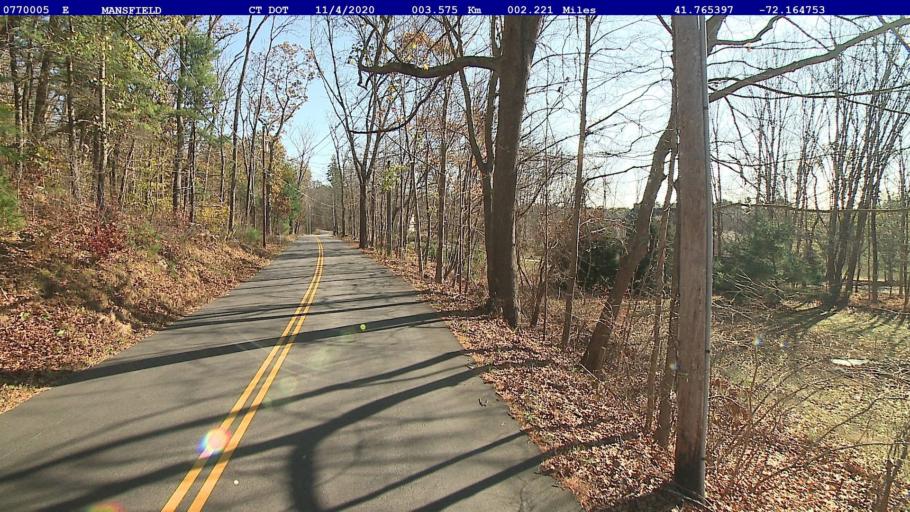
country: US
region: Connecticut
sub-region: Windham County
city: Windham
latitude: 41.7654
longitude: -72.1647
